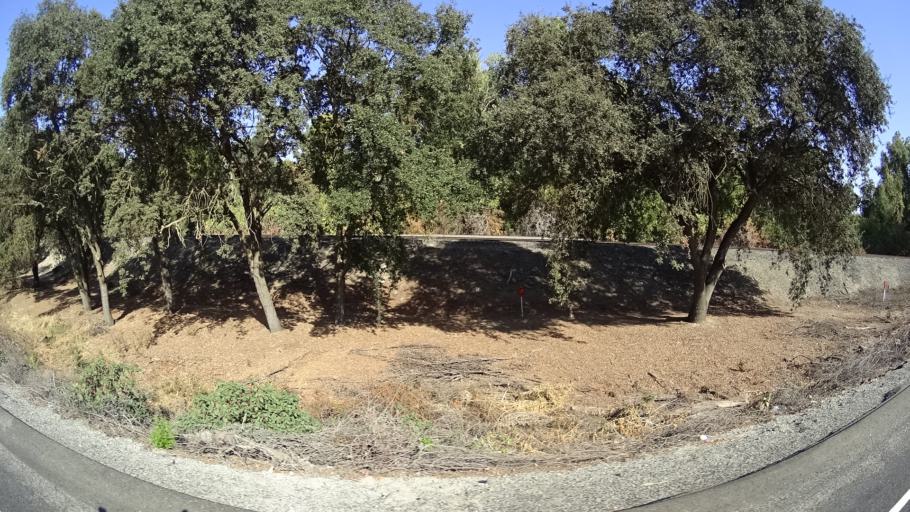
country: US
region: California
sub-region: Yolo County
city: West Sacramento
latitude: 38.6614
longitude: -121.6144
